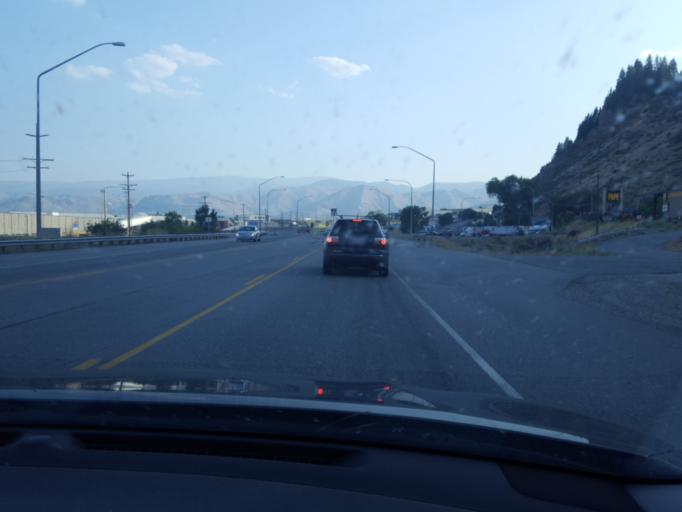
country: US
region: Washington
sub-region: Chelan County
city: Sunnyslope
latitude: 47.4820
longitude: -120.3201
